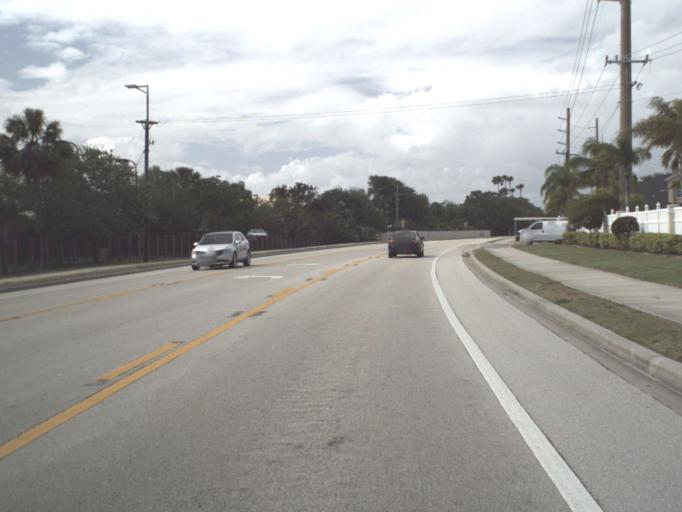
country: US
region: Florida
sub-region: Brevard County
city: Satellite Beach
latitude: 28.1621
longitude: -80.6051
